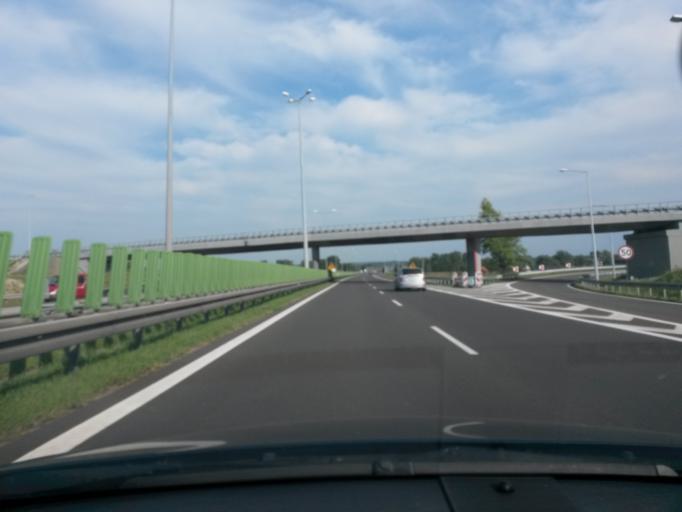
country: PL
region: Greater Poland Voivodeship
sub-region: Powiat koninski
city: Rzgow Pierwszy
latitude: 52.2053
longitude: 18.0204
